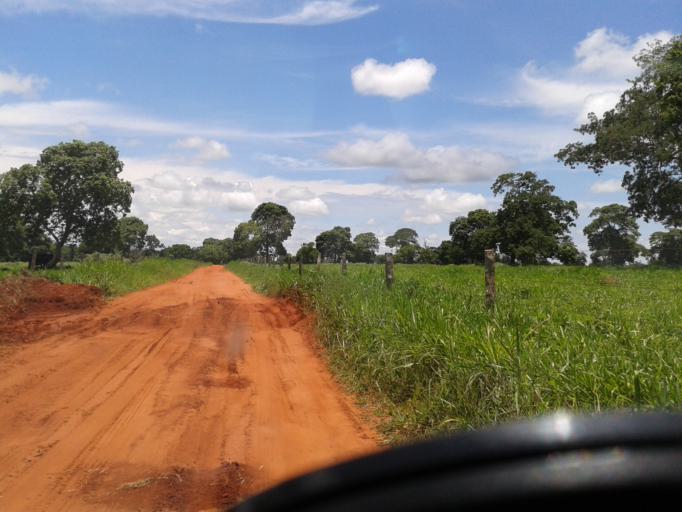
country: BR
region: Minas Gerais
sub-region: Santa Vitoria
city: Santa Vitoria
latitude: -18.9523
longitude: -49.8635
